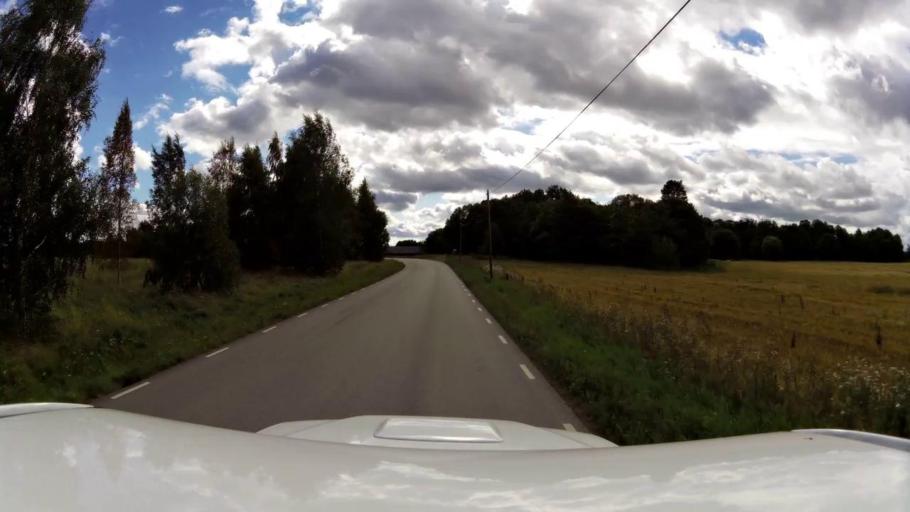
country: SE
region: OEstergoetland
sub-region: Linkopings Kommun
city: Linkoping
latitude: 58.3826
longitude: 15.5923
